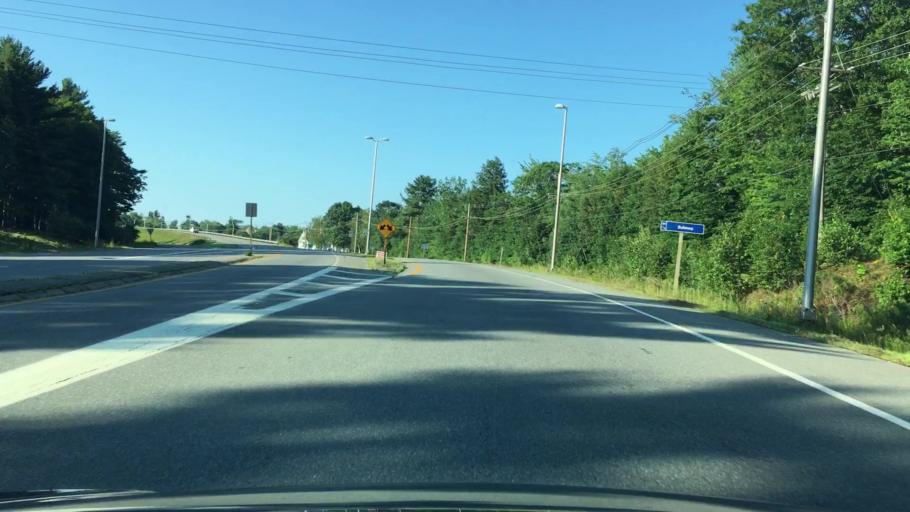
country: US
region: Maine
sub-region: Waldo County
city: Belfast
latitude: 44.4281
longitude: -69.0216
